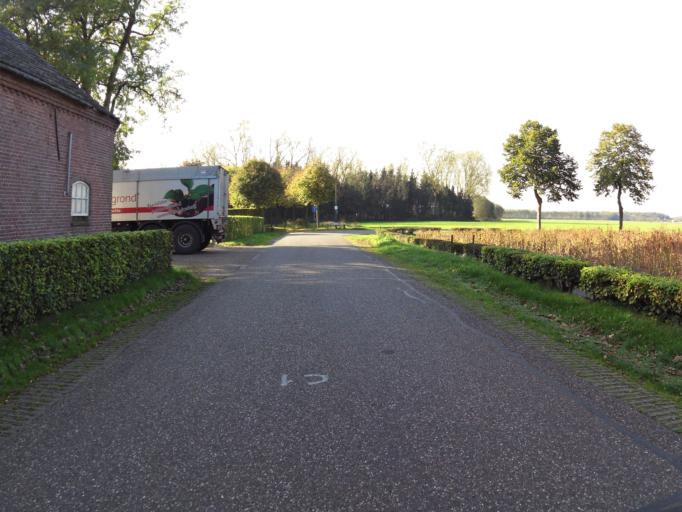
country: NL
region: North Brabant
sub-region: Gemeente Helmond
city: Helmond
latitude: 51.5187
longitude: 5.6912
